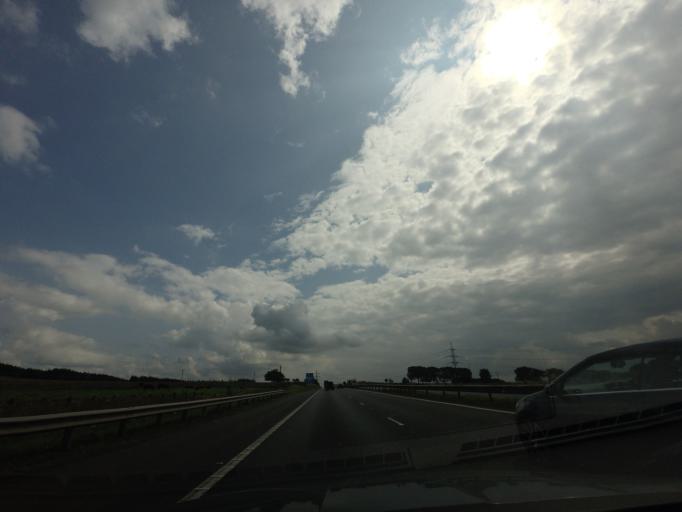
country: GB
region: Scotland
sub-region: South Lanarkshire
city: Lesmahagow
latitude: 55.6155
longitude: -3.8496
